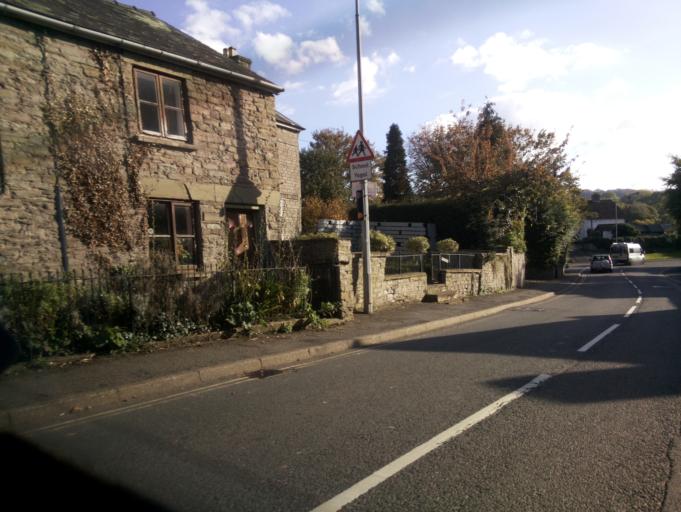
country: GB
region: Wales
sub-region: Sir Powys
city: Hay
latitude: 52.0719
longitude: -3.1291
